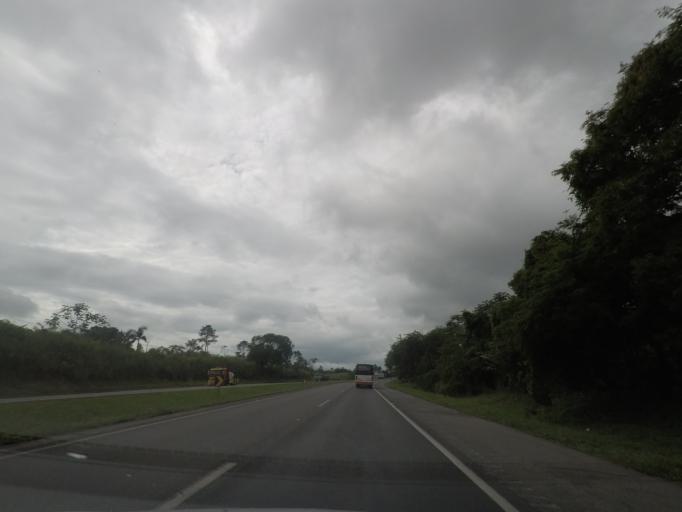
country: BR
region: Sao Paulo
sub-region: Miracatu
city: Miracatu
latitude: -24.2811
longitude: -47.4305
